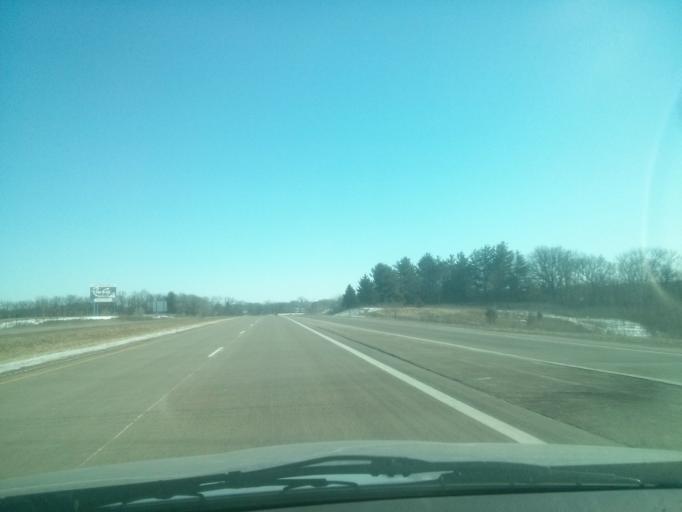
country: US
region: Wisconsin
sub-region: Saint Croix County
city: Somerset
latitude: 45.1222
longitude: -92.6509
